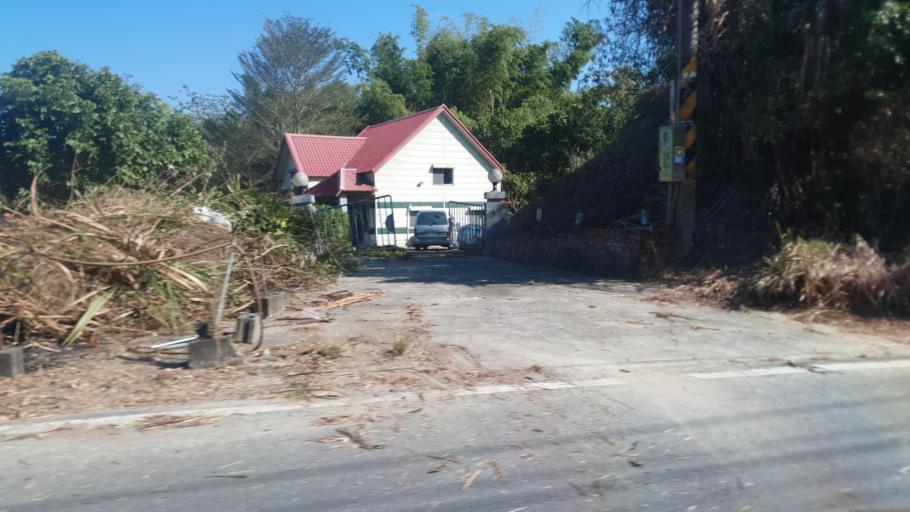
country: TW
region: Taiwan
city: Yujing
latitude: 23.0380
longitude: 120.3963
